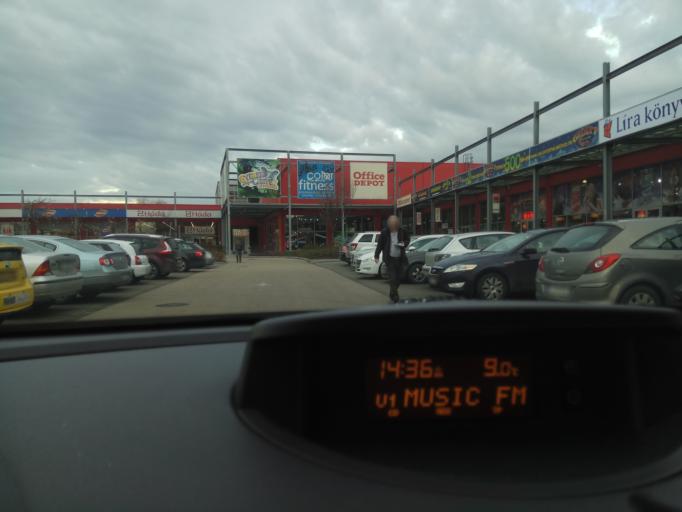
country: HU
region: Pest
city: Dunakeszi
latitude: 47.6097
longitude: 19.1193
